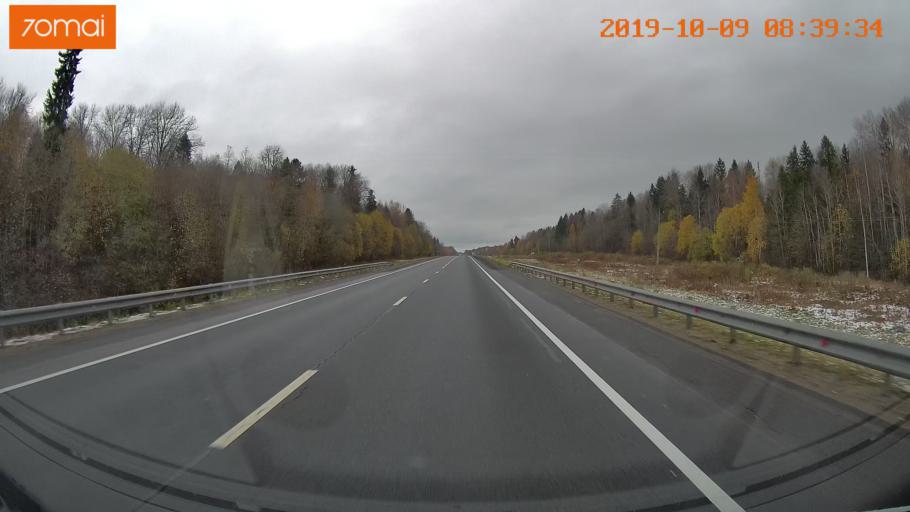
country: RU
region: Vologda
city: Gryazovets
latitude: 58.9734
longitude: 40.1515
